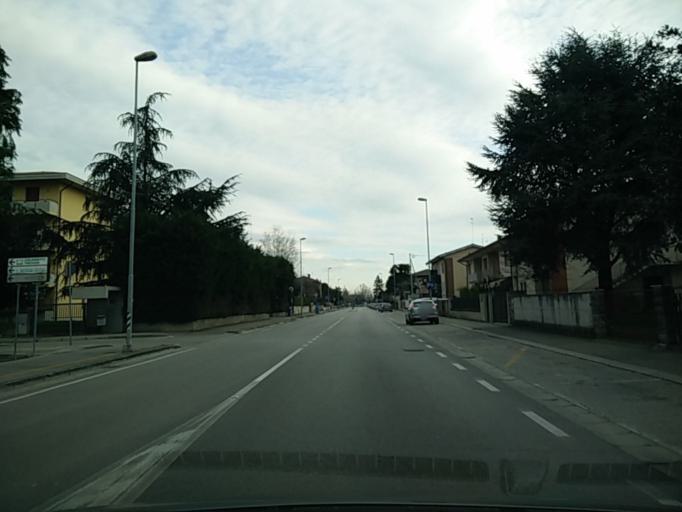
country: IT
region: Veneto
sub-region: Provincia di Treviso
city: Paese
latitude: 45.6710
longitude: 12.1770
